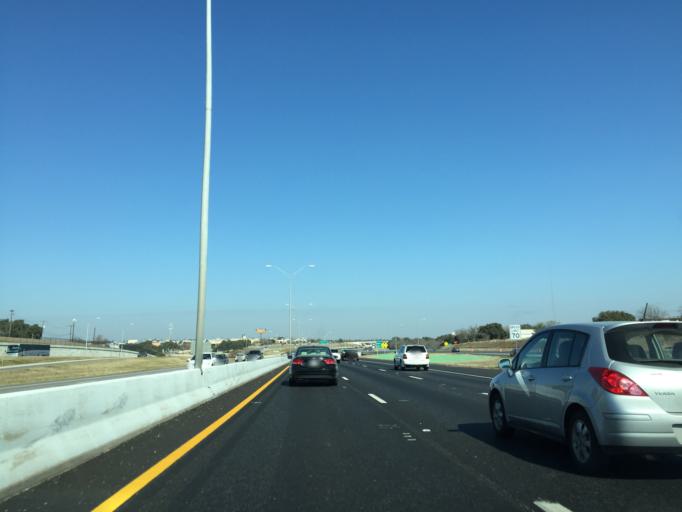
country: US
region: Texas
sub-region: Williamson County
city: Georgetown
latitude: 30.6227
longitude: -97.6901
